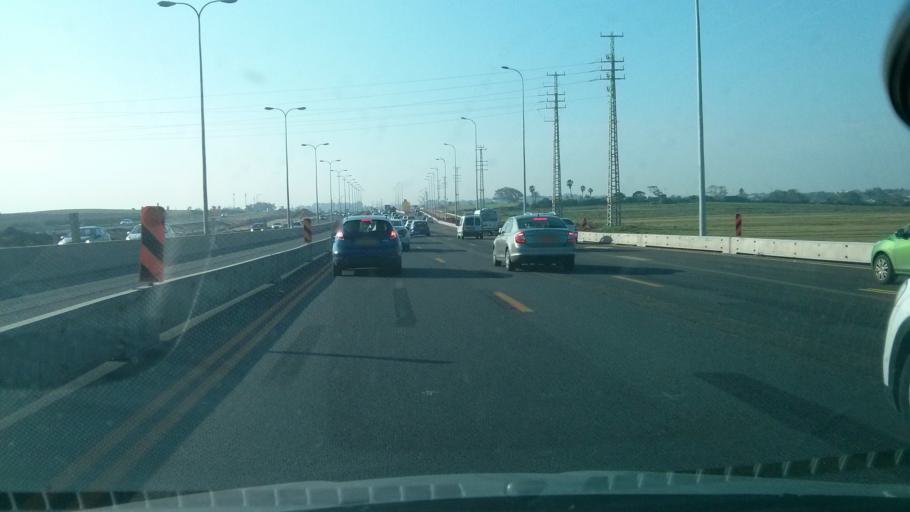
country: IL
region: Tel Aviv
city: Kefar Shemaryahu
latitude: 32.2396
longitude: 34.8334
